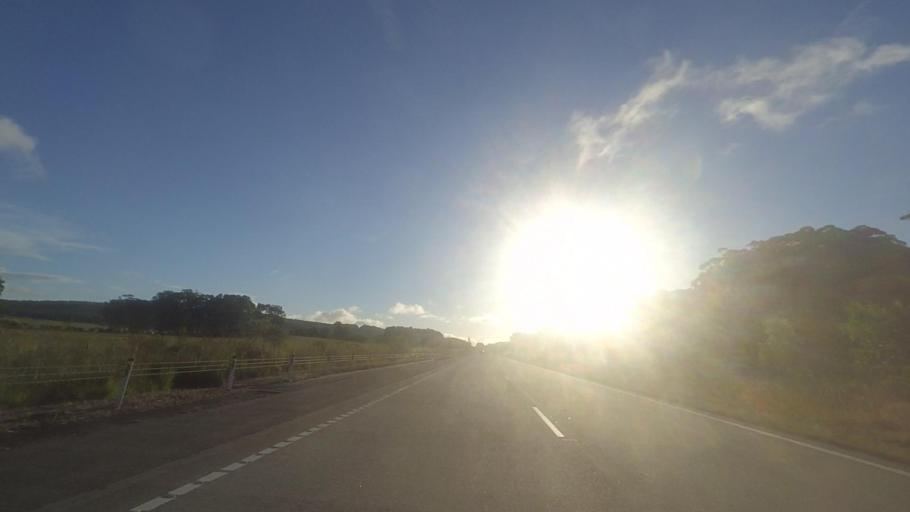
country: AU
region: New South Wales
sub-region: Great Lakes
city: Bulahdelah
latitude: -32.5234
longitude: 152.1991
